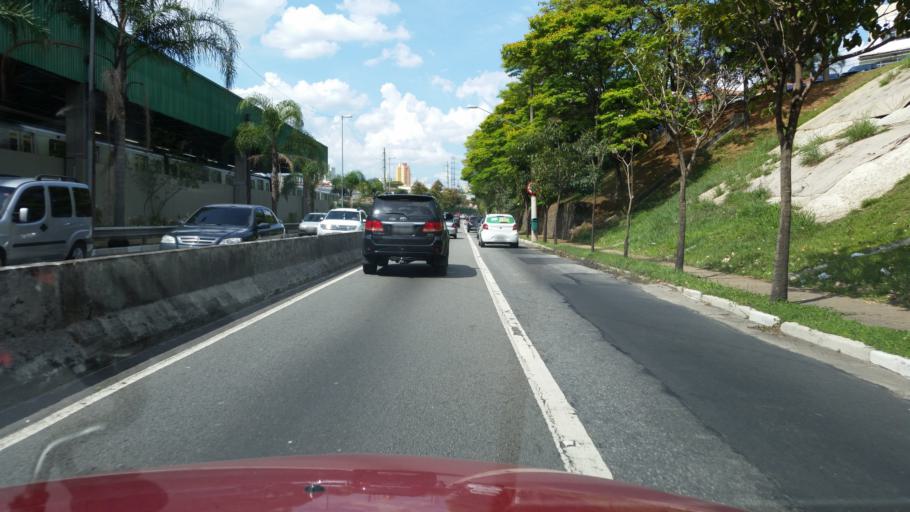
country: BR
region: Sao Paulo
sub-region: Guarulhos
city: Guarulhos
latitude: -23.5296
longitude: -46.5166
